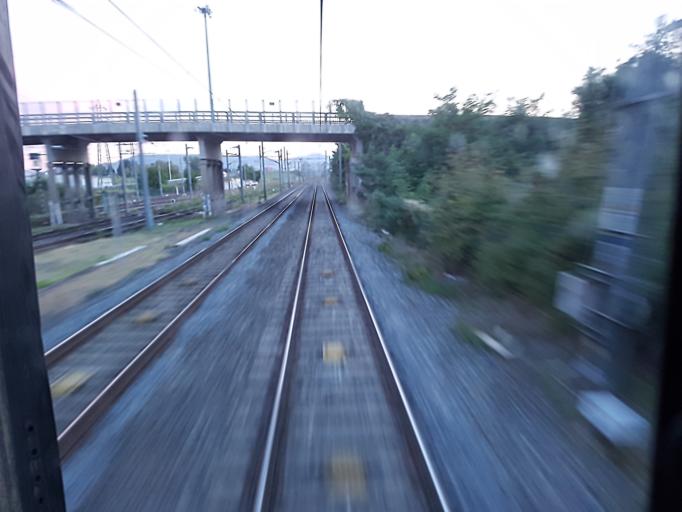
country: FR
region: Auvergne
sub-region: Departement du Puy-de-Dome
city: Gerzat
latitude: 45.8120
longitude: 3.1324
